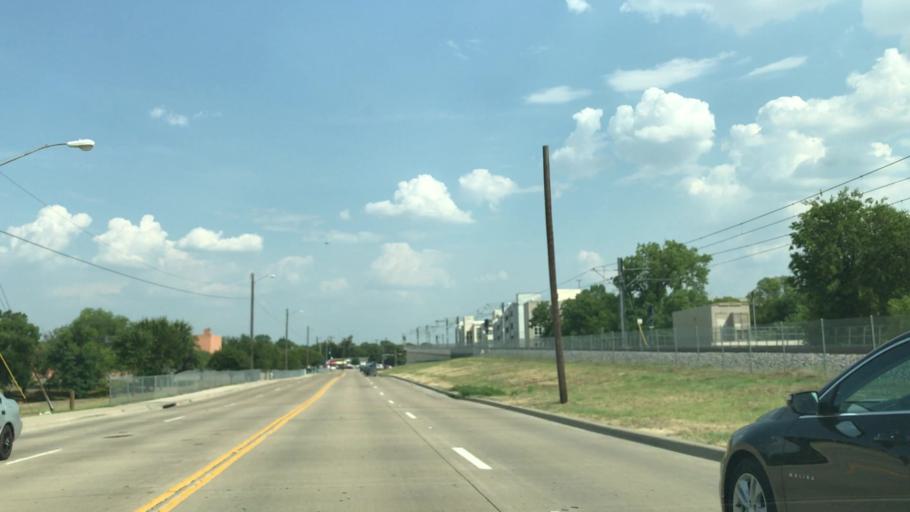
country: US
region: Texas
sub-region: Dallas County
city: University Park
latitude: 32.8262
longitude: -96.8369
